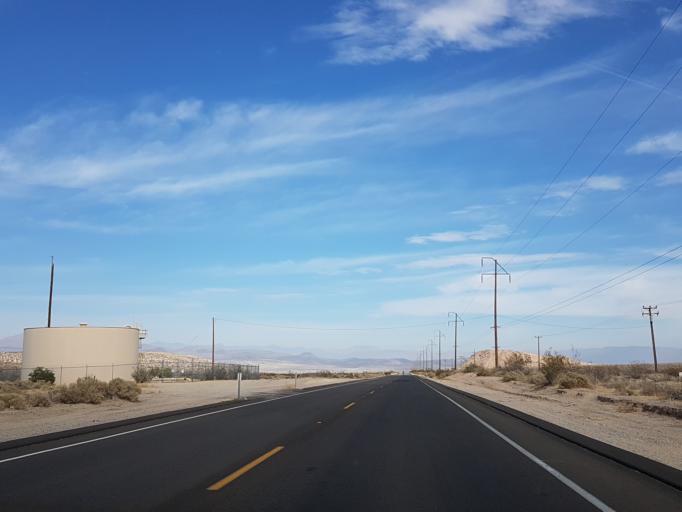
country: US
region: California
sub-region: Kern County
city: Ridgecrest
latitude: 35.6253
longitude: -117.5924
